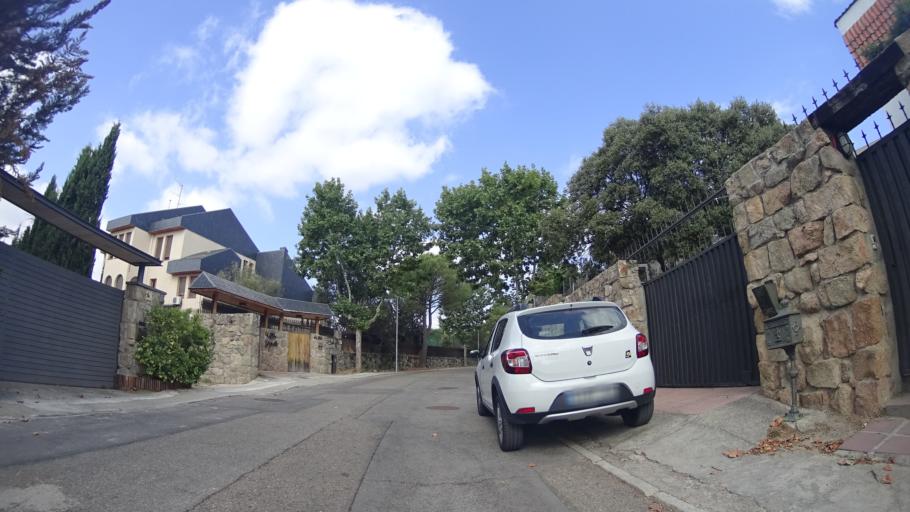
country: ES
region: Madrid
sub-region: Provincia de Madrid
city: Torrelodones
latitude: 40.5879
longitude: -3.9179
